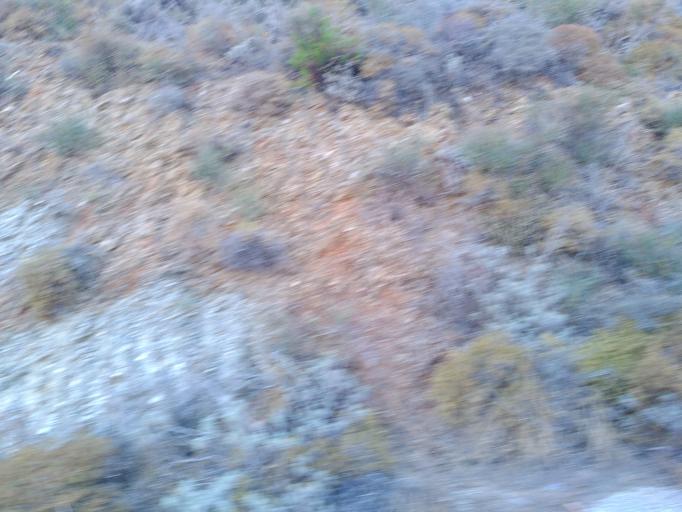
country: GR
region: South Aegean
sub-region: Nomos Kykladon
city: Amorgos
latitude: 36.9121
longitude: 25.9773
